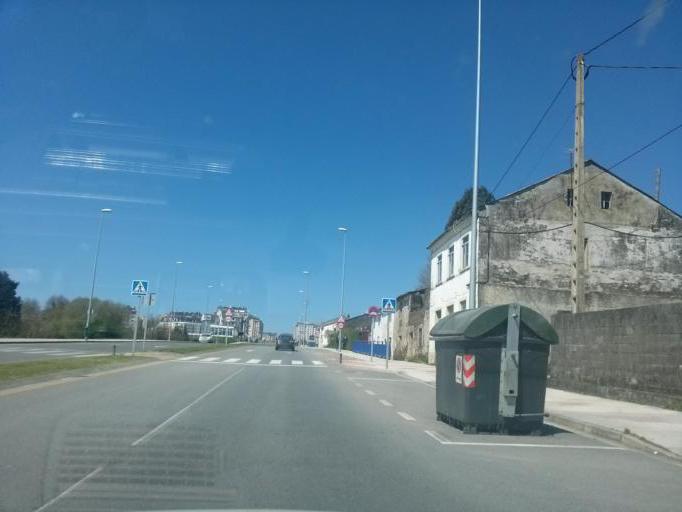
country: ES
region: Galicia
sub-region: Provincia de Lugo
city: Lugo
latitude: 42.9940
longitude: -7.5424
